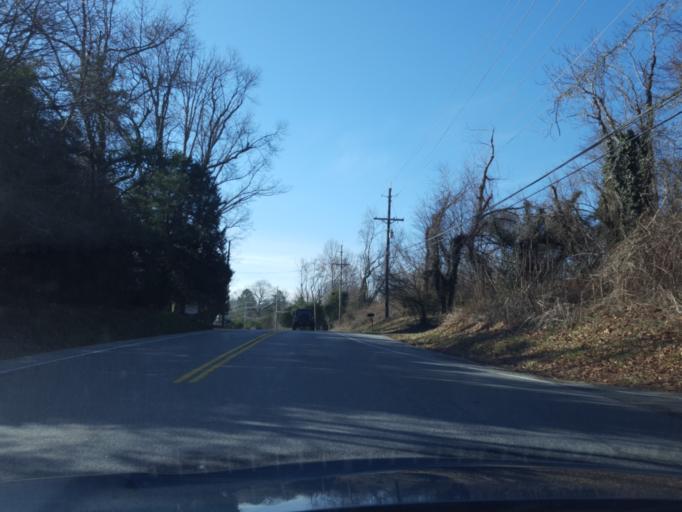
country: US
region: Maryland
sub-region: Calvert County
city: Prince Frederick
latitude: 38.4781
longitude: -76.5462
